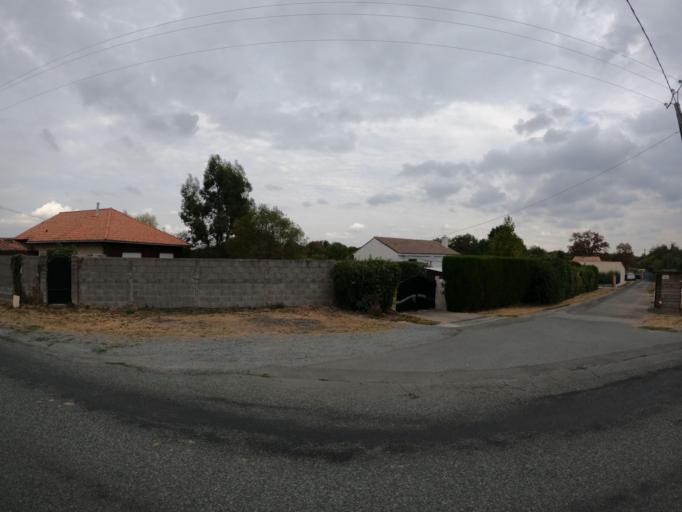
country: FR
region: Pays de la Loire
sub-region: Departement de Maine-et-Loire
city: Le Longeron
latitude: 47.0295
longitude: -1.0468
